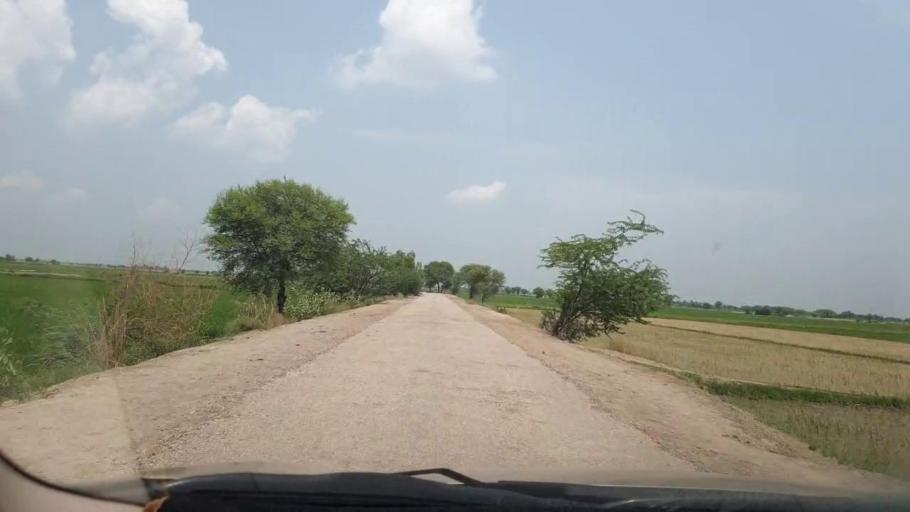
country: PK
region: Sindh
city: Larkana
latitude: 27.6029
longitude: 68.1431
